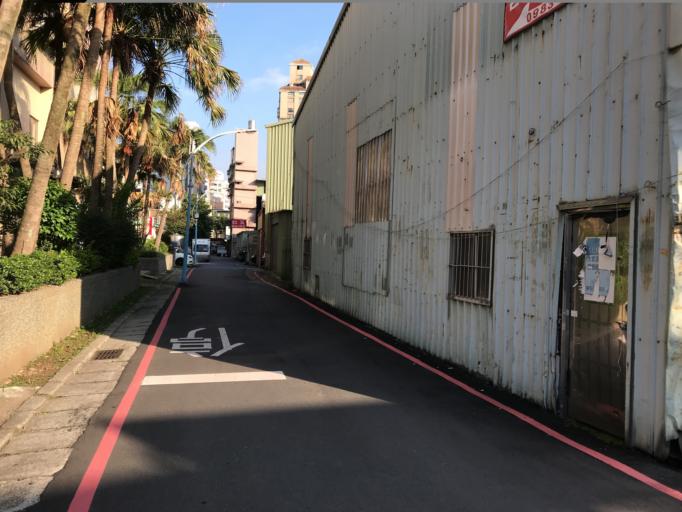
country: TW
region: Taiwan
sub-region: Taoyuan
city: Taoyuan
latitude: 24.9290
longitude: 121.3714
